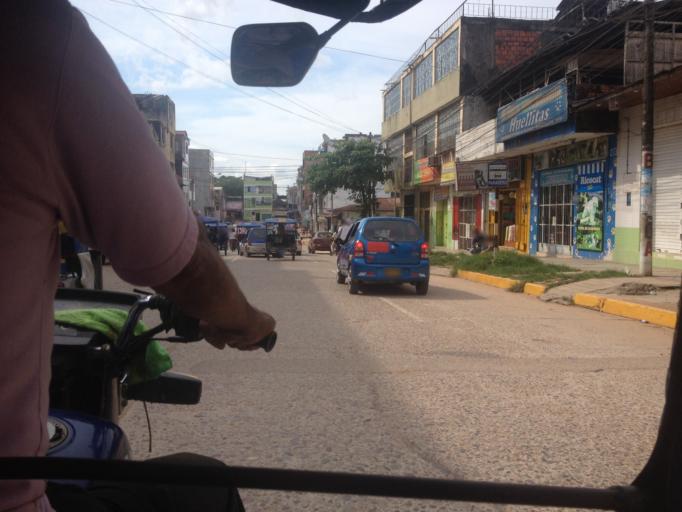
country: PE
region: Ucayali
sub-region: Provincia de Coronel Portillo
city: Pucallpa
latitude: -8.3833
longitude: -74.5349
